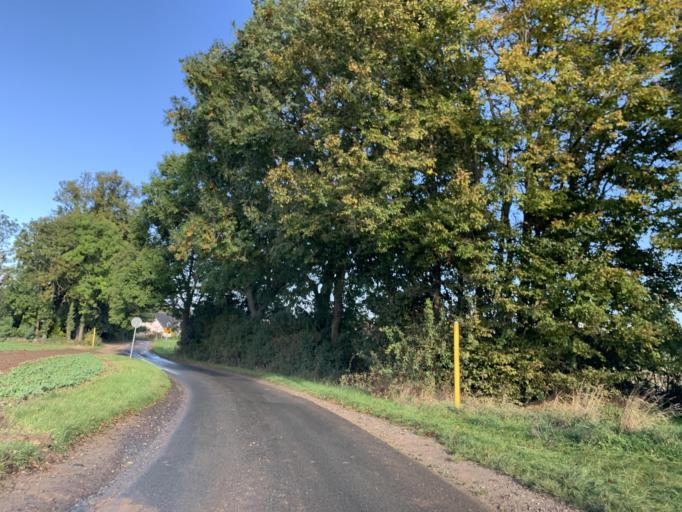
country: DE
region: Mecklenburg-Vorpommern
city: Burg Stargard
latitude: 53.4626
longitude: 13.2747
